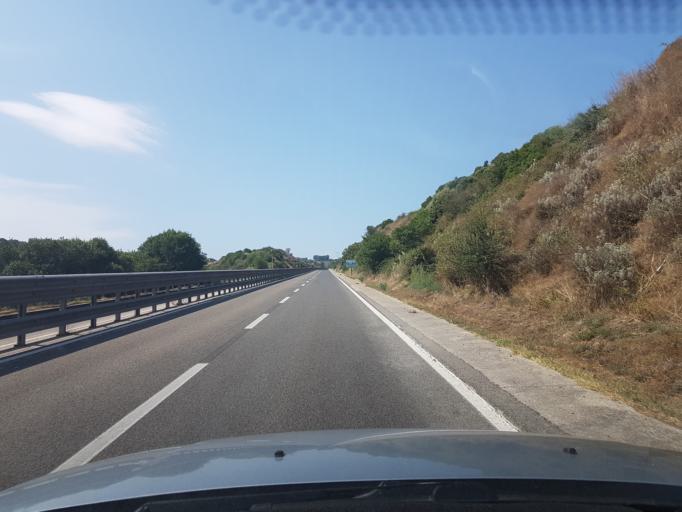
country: IT
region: Sardinia
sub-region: Provincia di Oristano
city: Soddi
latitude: 40.1387
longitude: 8.8703
